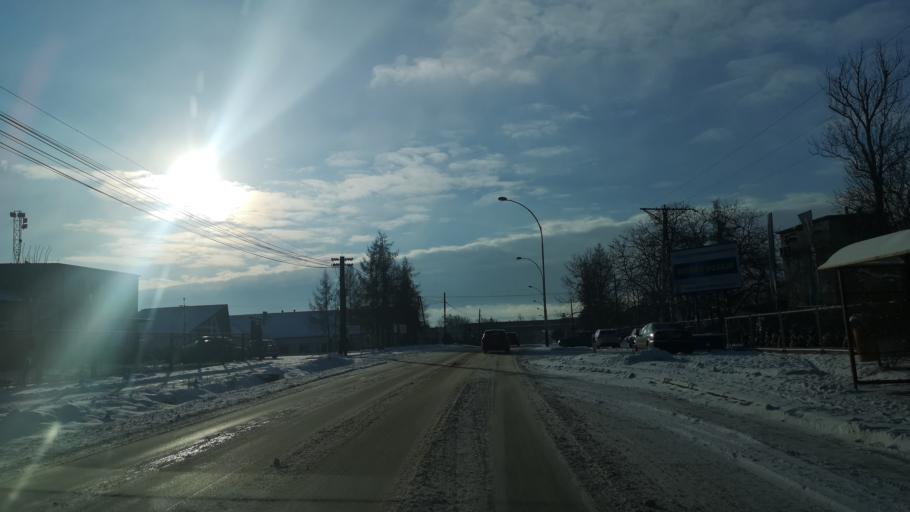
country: PL
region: Subcarpathian Voivodeship
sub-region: Powiat przeworski
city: Gorliczyna
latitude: 50.0850
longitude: 22.4928
